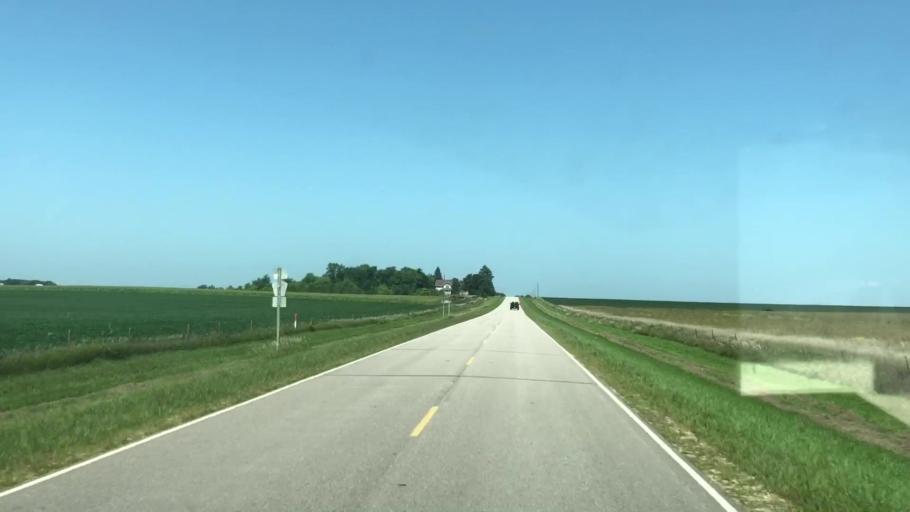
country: US
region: Iowa
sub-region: O'Brien County
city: Sanborn
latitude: 43.2450
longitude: -95.7234
